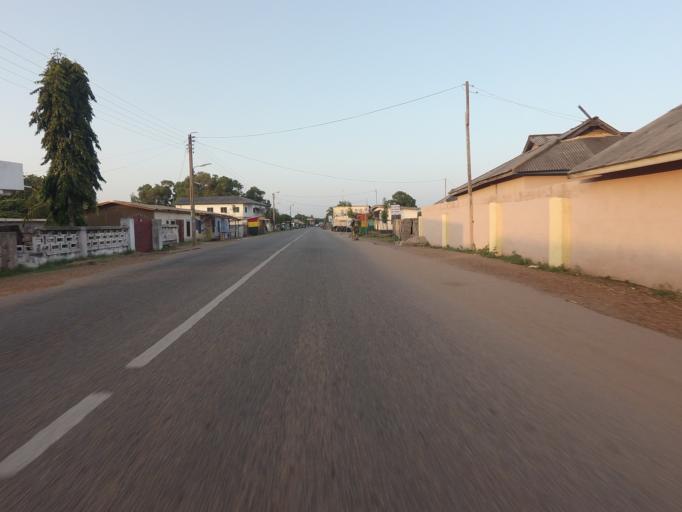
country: GH
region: Volta
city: Anloga
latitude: 5.7945
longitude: 0.9021
